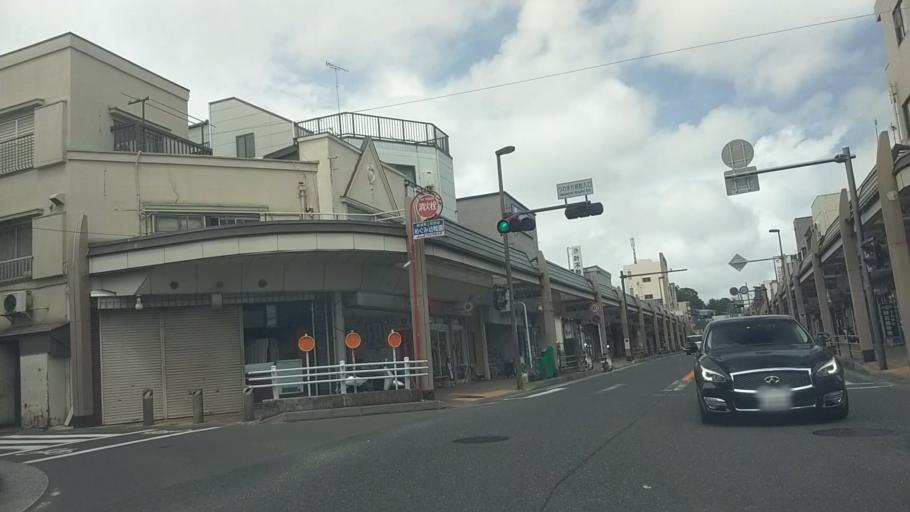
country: JP
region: Kanagawa
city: Yokosuka
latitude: 35.2726
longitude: 139.6705
